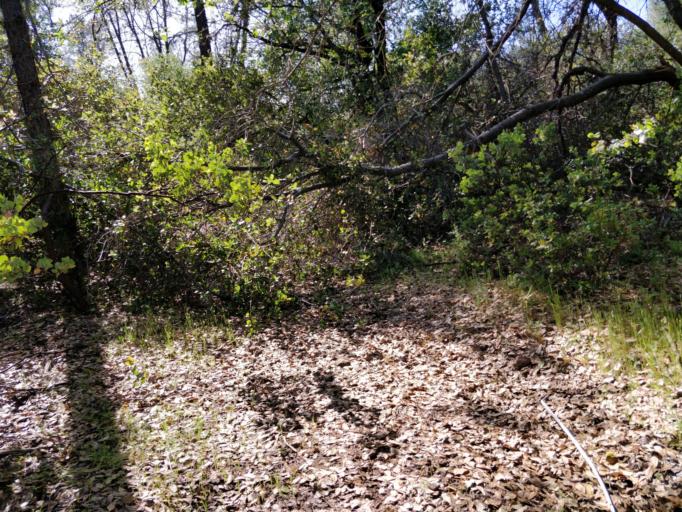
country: US
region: California
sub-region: Shasta County
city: Shasta Lake
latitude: 40.6674
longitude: -122.3687
